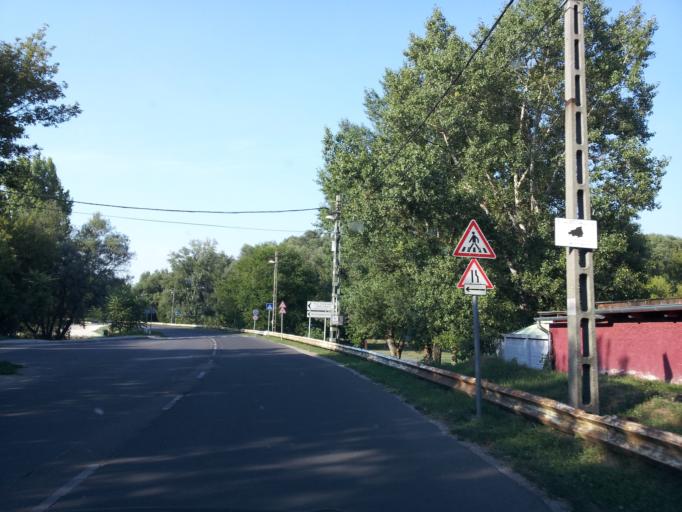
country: HU
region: Pest
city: Szentendre
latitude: 47.6614
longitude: 19.0793
